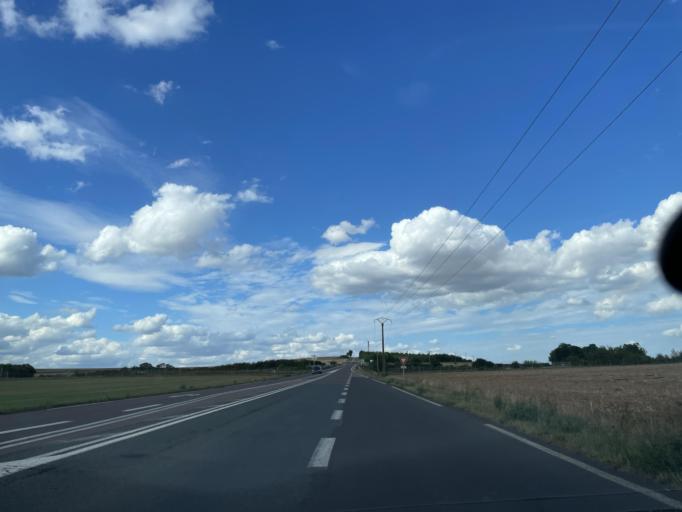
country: FR
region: Bourgogne
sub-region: Departement de l'Yonne
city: Sergines
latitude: 48.3225
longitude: 3.2253
